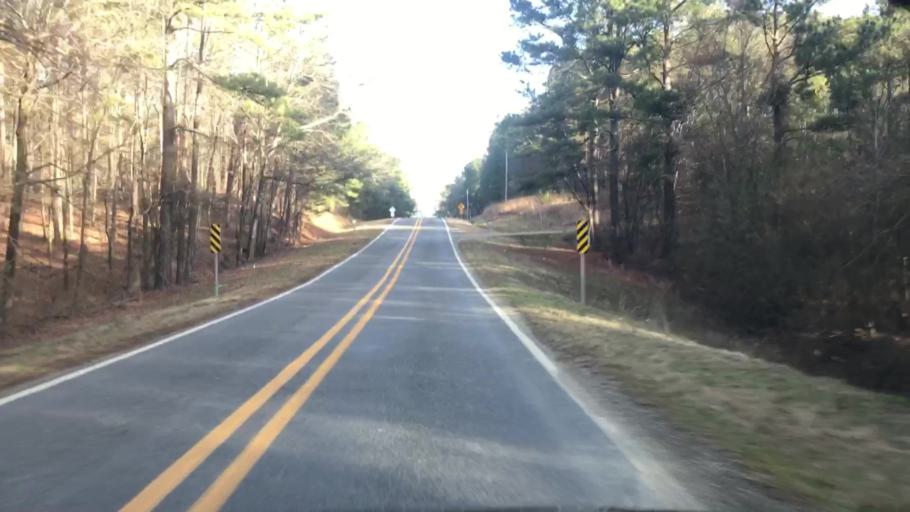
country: US
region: Arkansas
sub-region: Garland County
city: Rockwell
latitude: 34.4836
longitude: -93.2732
